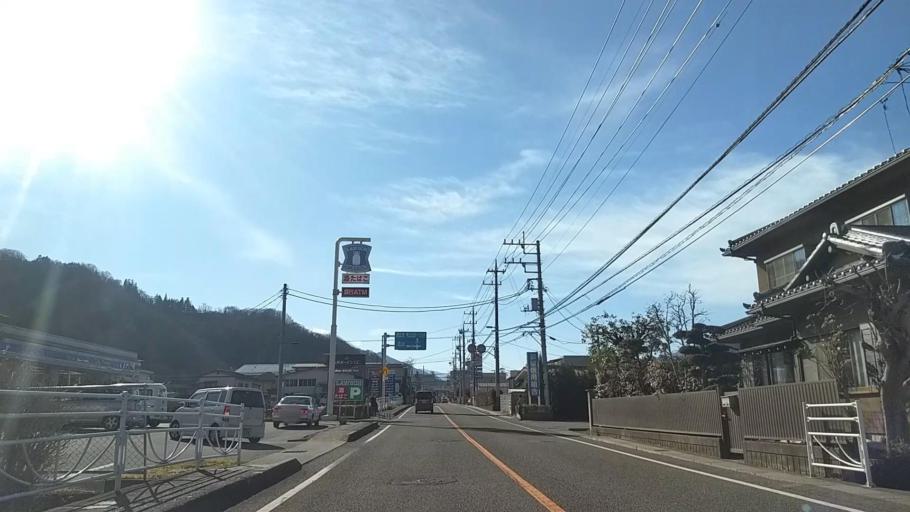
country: JP
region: Yamanashi
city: Otsuki
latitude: 35.5761
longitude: 138.9315
